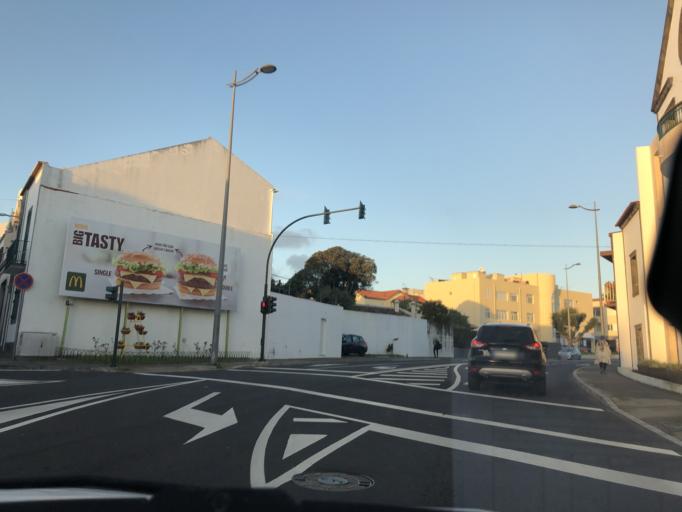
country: PT
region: Azores
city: Ponta Delgada
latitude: 37.7474
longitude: -25.6666
